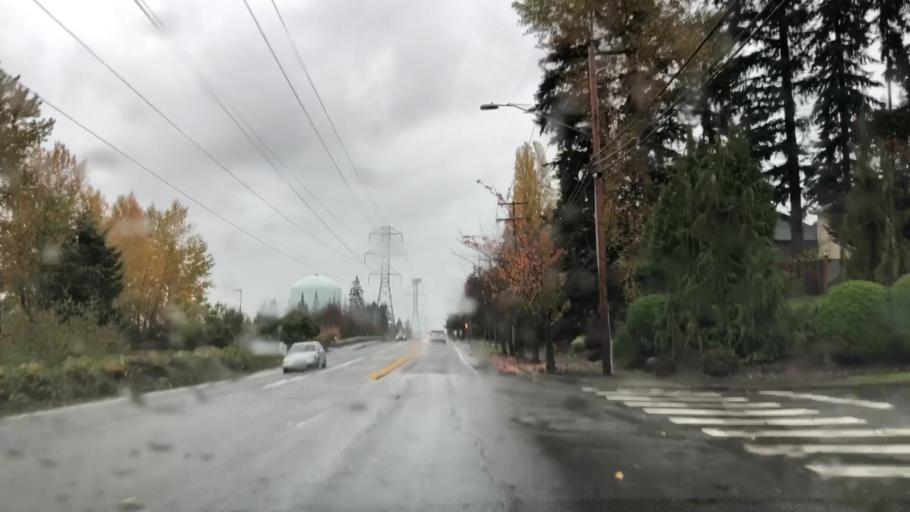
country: US
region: Washington
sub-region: King County
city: Kingsgate
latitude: 47.7396
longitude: -122.1751
